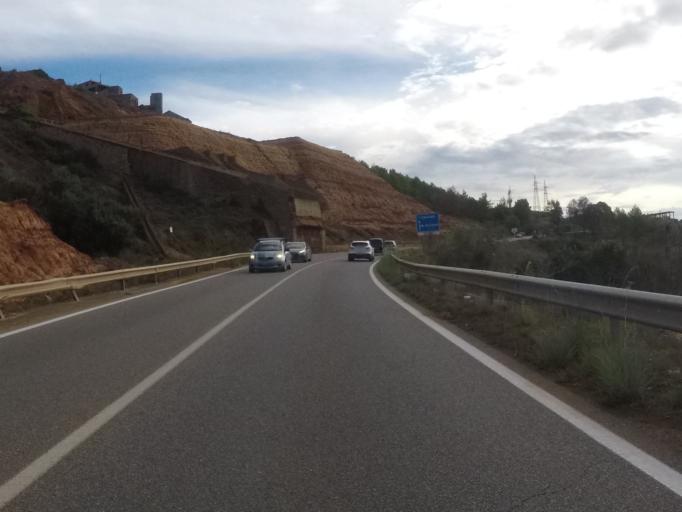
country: IT
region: Sardinia
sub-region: Provincia di Carbonia-Iglesias
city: Iglesias
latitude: 39.2982
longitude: 8.5067
